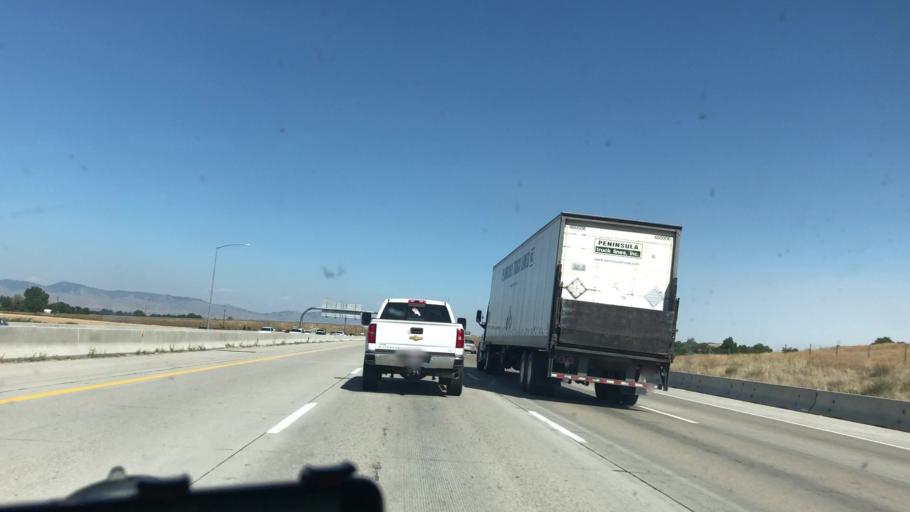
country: US
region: Idaho
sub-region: Canyon County
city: Nampa
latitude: 43.5995
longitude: -116.5006
